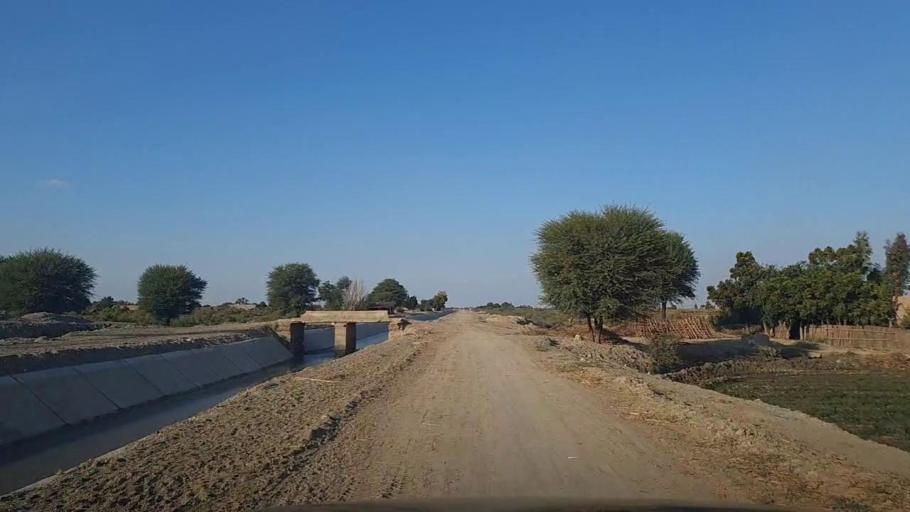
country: PK
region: Sindh
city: Jhol
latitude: 25.9111
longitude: 69.0402
